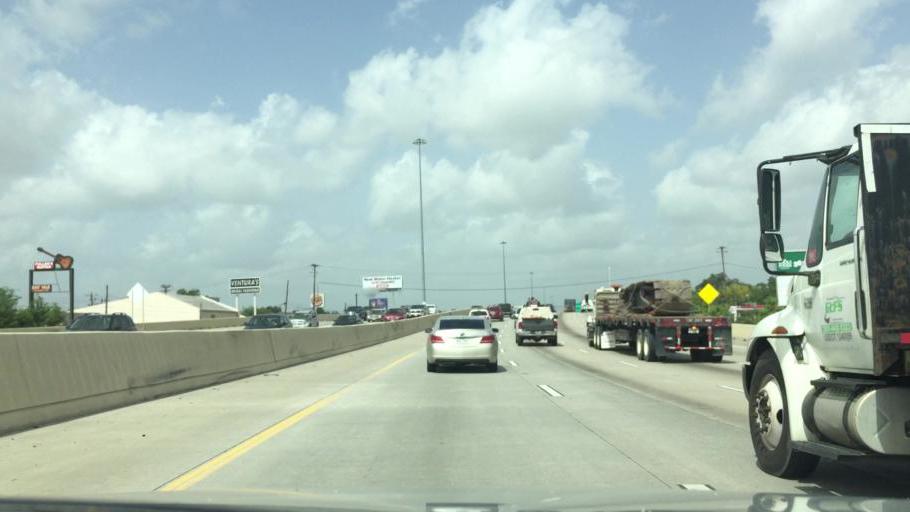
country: US
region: Texas
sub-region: Harris County
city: Houston
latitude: 29.8134
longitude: -95.3977
